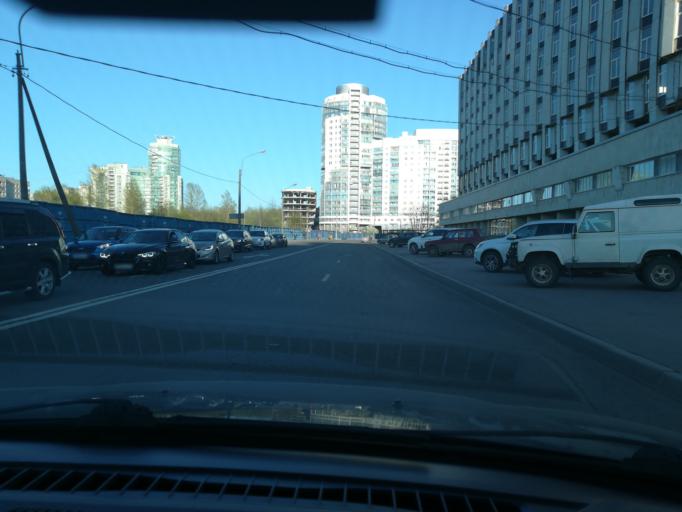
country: RU
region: St.-Petersburg
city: Vasyl'evsky Ostrov
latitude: 59.9470
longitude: 30.2319
